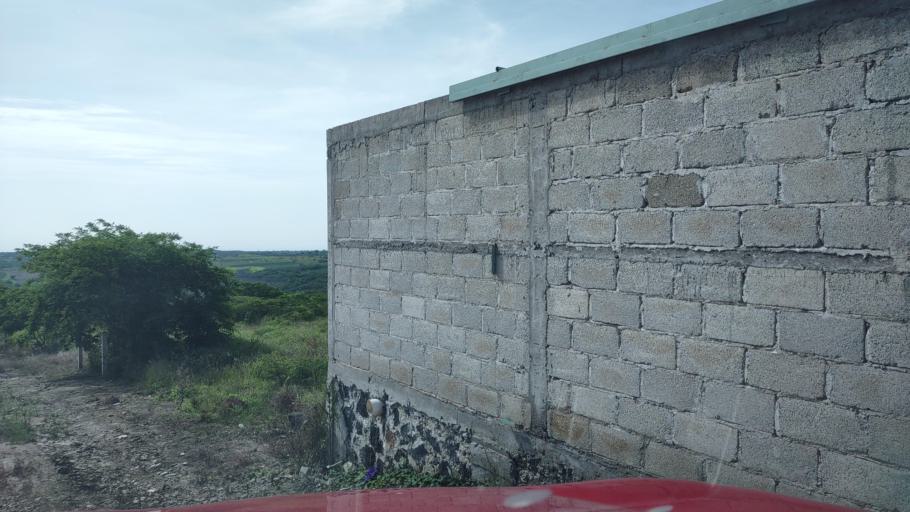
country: MX
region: Veracruz
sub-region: Emiliano Zapata
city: Dos Rios
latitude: 19.4710
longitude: -96.8225
